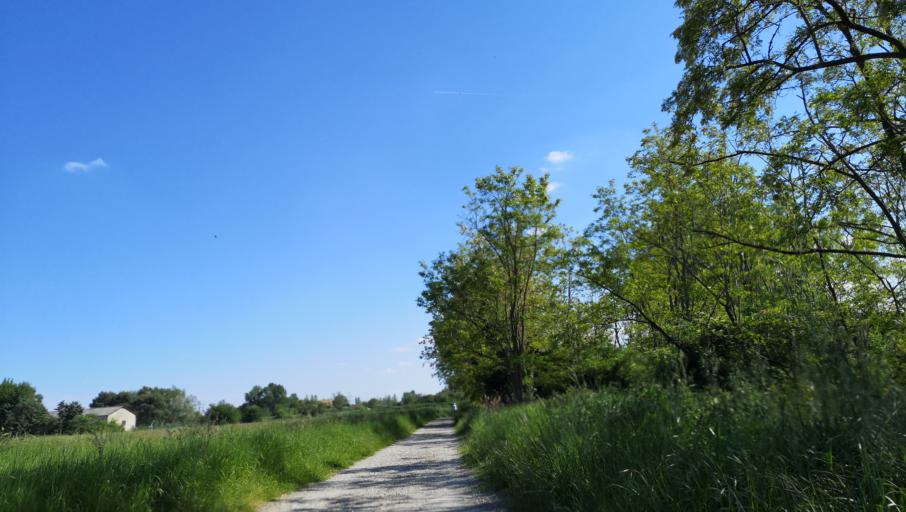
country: FR
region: Midi-Pyrenees
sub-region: Departement de la Haute-Garonne
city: Aucamville
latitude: 43.6608
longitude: 1.4069
